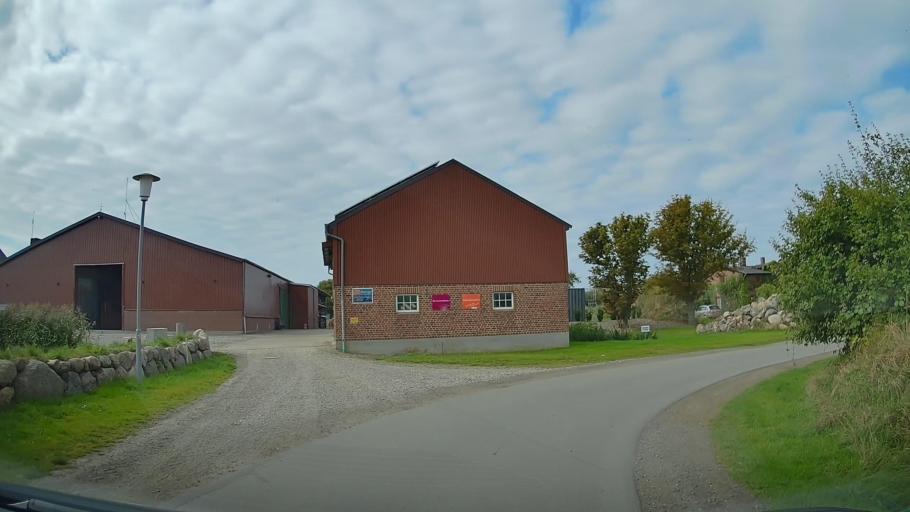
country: DE
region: Schleswig-Holstein
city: Grossenbrode
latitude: 54.5224
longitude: 11.0535
